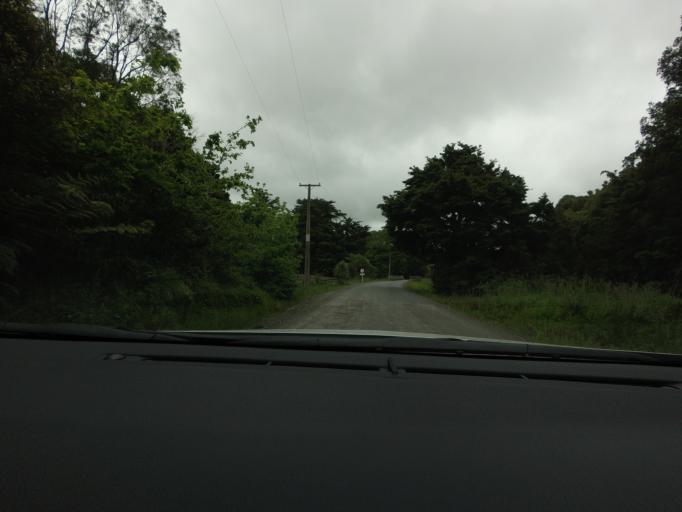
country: NZ
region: Auckland
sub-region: Auckland
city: Warkworth
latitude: -36.4798
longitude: 174.5605
